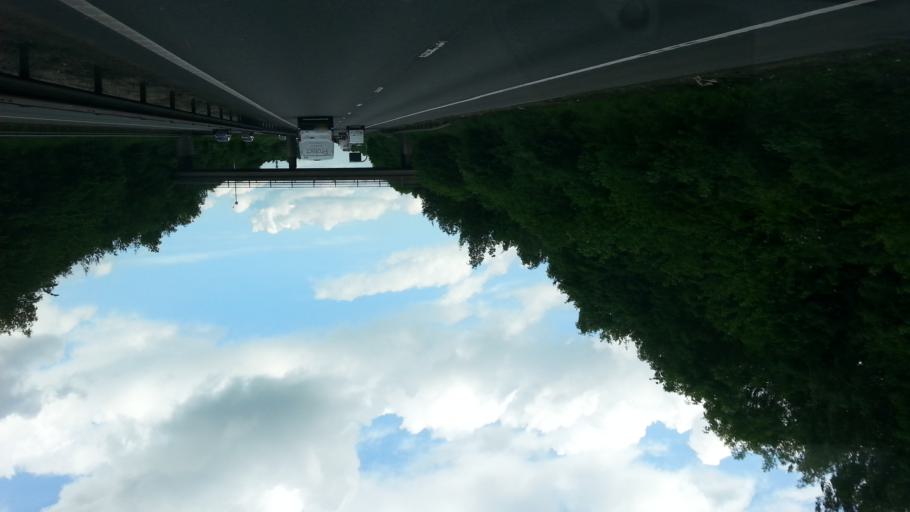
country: GB
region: England
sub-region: Staffordshire
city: Fazeley
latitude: 52.6095
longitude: -1.6363
